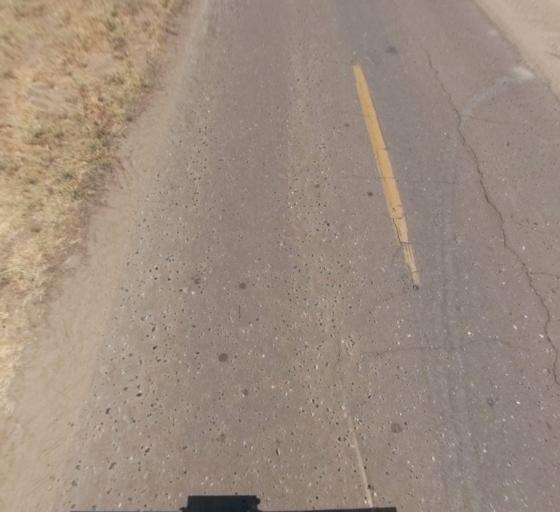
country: US
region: California
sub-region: Fresno County
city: Biola
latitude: 36.8277
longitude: -120.0428
